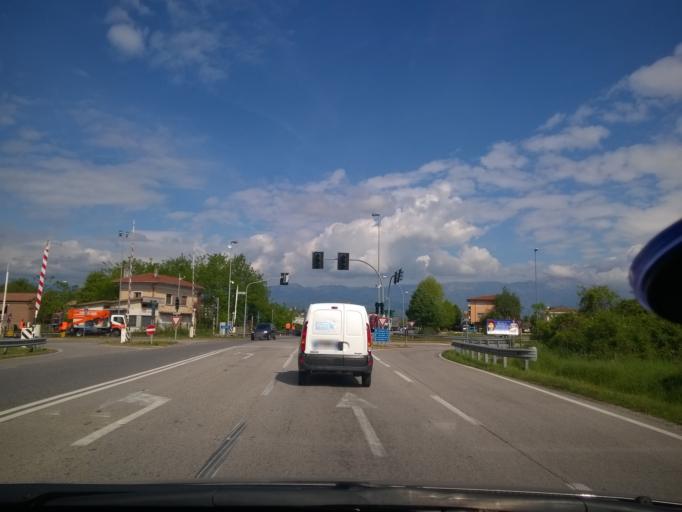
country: IT
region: Veneto
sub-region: Provincia di Treviso
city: San Vendemiano-Fossamerlo
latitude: 45.9016
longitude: 12.3298
